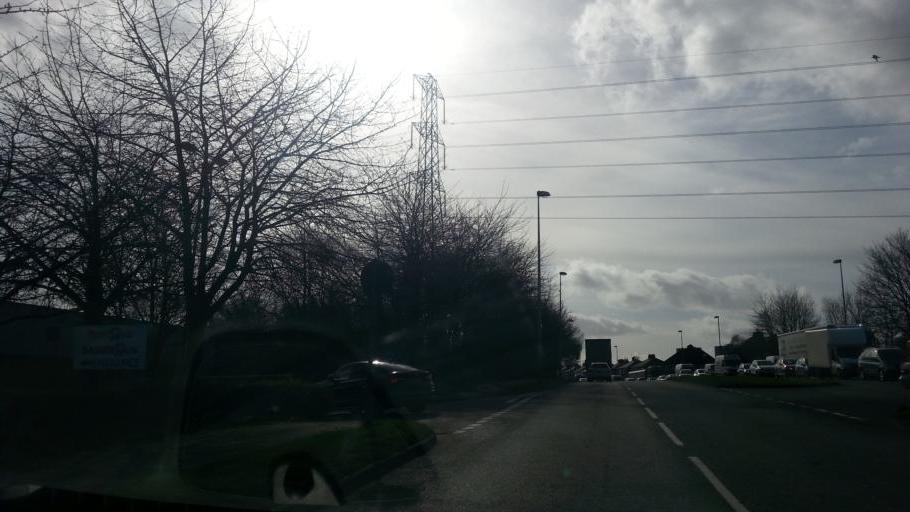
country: GB
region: England
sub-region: Sandwell
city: Oldbury
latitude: 52.4922
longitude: -2.0237
